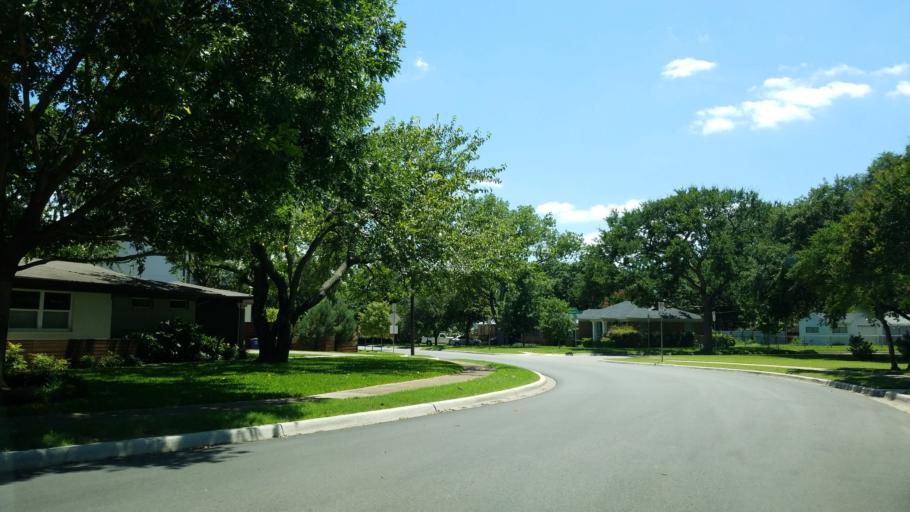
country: US
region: Texas
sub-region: Dallas County
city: University Park
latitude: 32.8789
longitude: -96.8463
